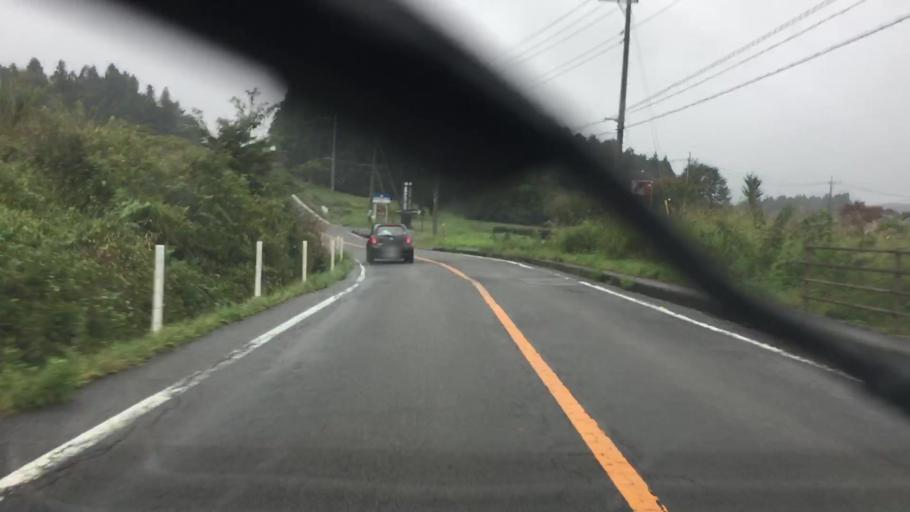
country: JP
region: Yamanashi
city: Fujikawaguchiko
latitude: 35.4030
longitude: 138.6130
